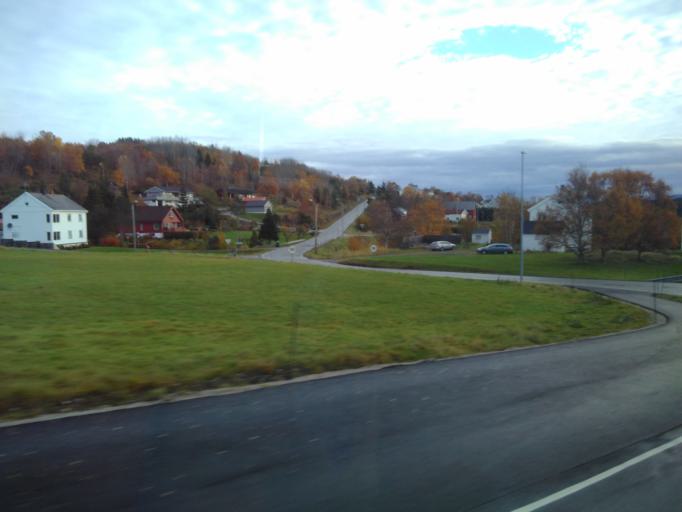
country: NO
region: Sor-Trondelag
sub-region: Hitra
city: Fillan
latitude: 63.5224
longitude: 9.0945
